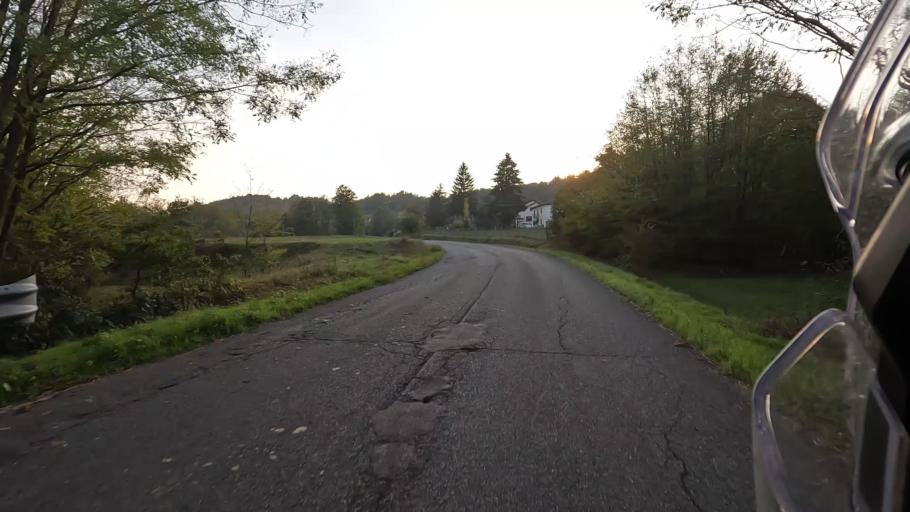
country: IT
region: Liguria
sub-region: Provincia di Savona
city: Mioglia
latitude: 44.5103
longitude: 8.4379
